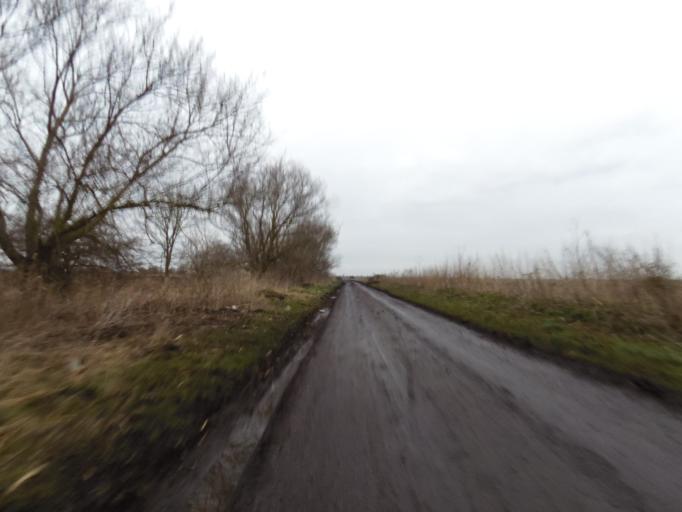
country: GB
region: England
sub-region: Cambridgeshire
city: Bottisham
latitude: 52.2804
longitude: 0.2674
